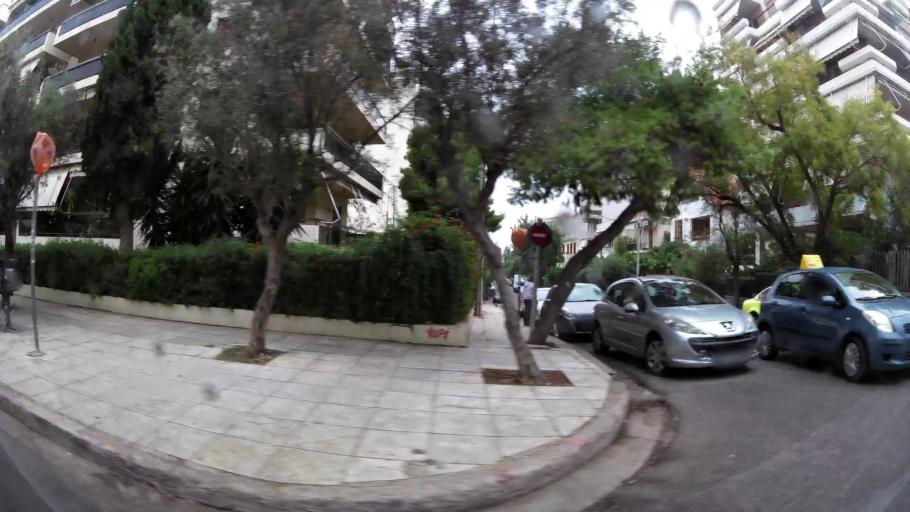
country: GR
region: Attica
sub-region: Nomarchia Athinas
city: Palaio Faliro
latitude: 37.9278
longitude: 23.6973
